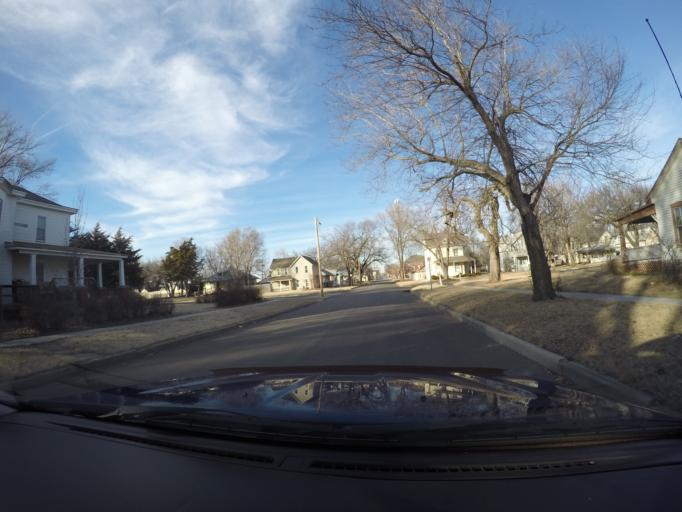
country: US
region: Kansas
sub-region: Harvey County
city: Newton
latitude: 38.0436
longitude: -97.3430
